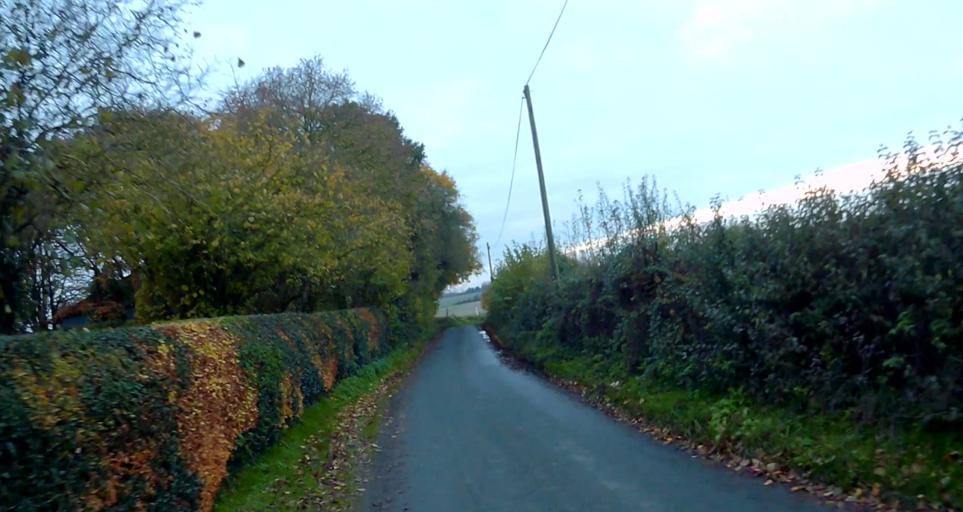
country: GB
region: England
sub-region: Hampshire
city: Odiham
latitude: 51.2501
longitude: -0.9230
